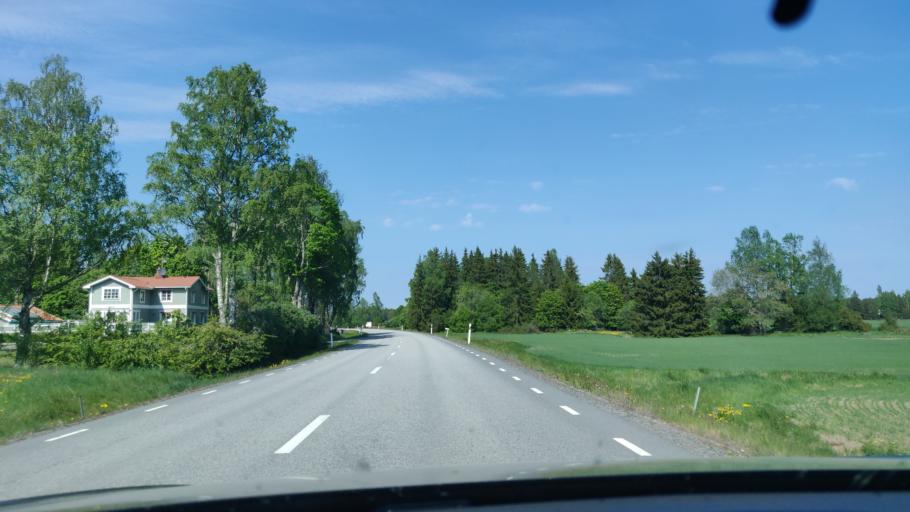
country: SE
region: Uppsala
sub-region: Heby Kommun
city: OEstervala
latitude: 60.1544
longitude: 17.2034
